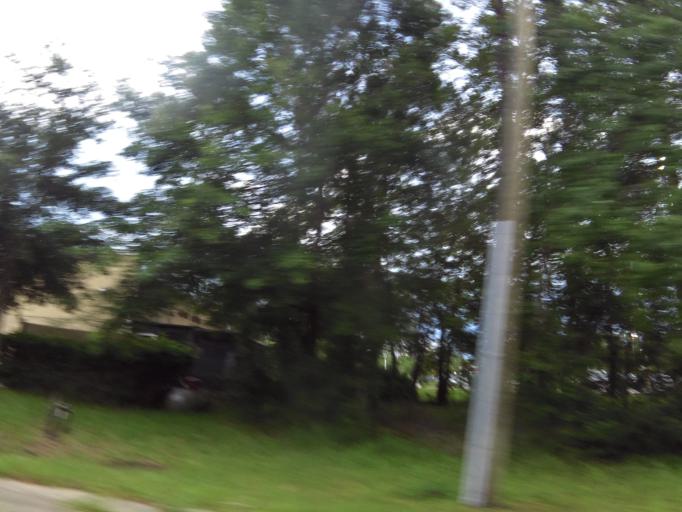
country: US
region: Florida
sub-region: Duval County
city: Jacksonville
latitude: 30.3231
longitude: -81.7877
